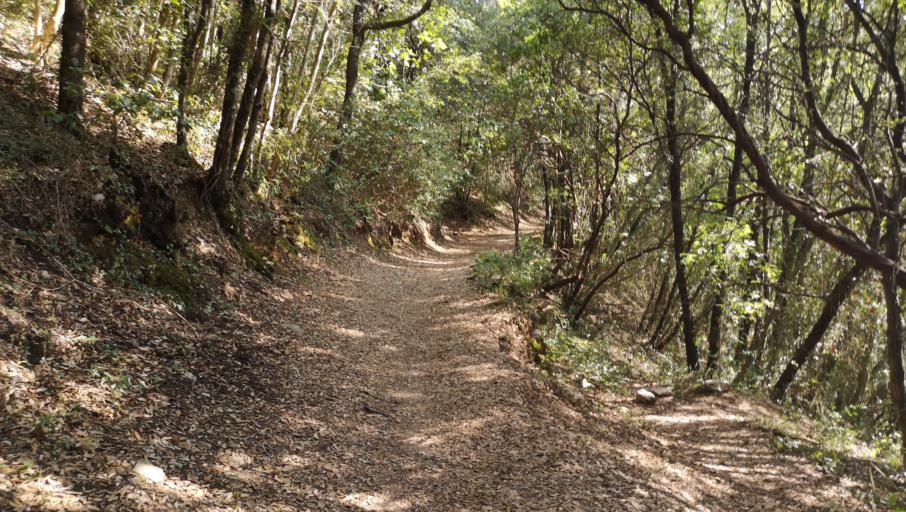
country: IT
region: Umbria
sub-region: Provincia di Terni
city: Narni
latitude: 42.5083
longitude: 12.5355
